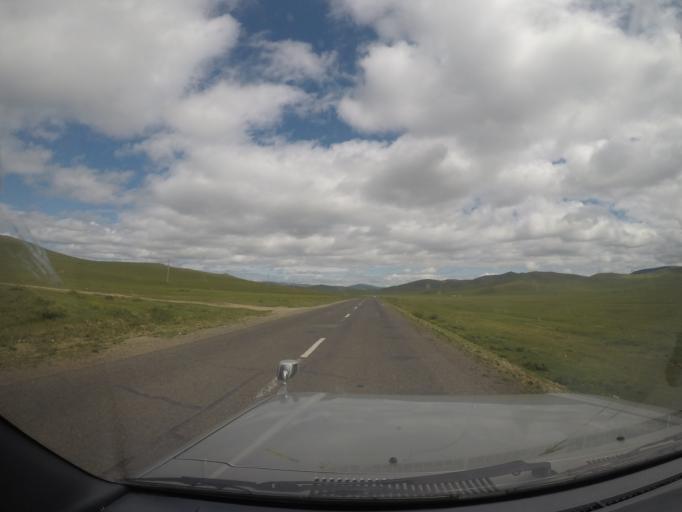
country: MN
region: Hentiy
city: Modot
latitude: 47.7661
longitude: 108.8934
